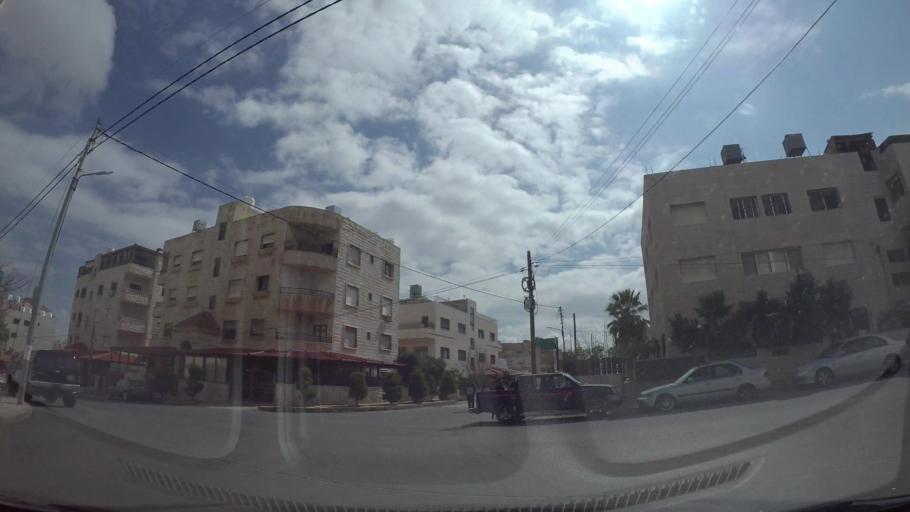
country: JO
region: Amman
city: Wadi as Sir
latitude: 31.9598
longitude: 35.8403
